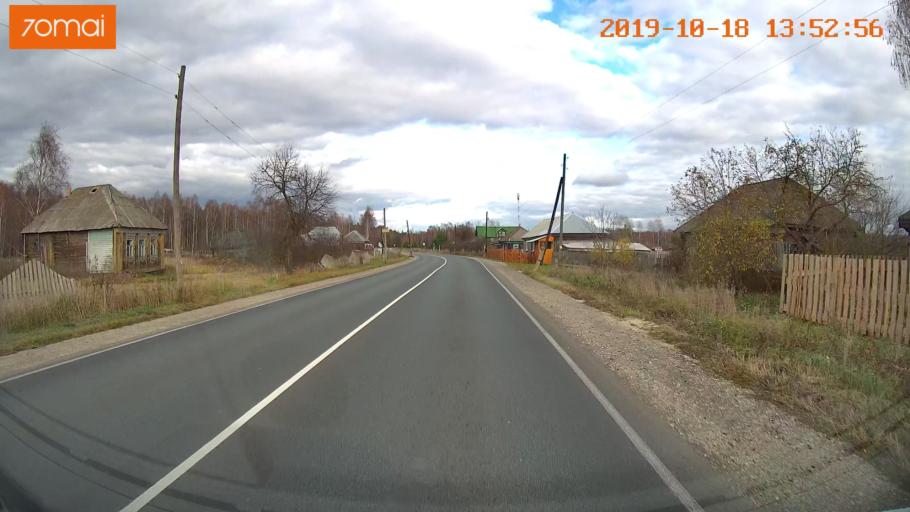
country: RU
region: Moskovskaya
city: Radovitskiy
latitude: 55.0339
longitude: 39.9727
